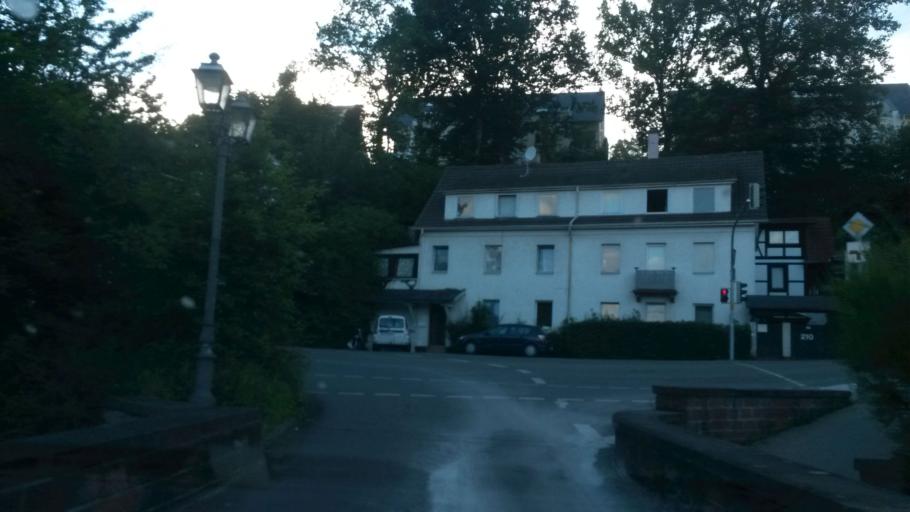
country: DE
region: Baden-Wuerttemberg
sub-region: Karlsruhe Region
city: Pforzheim
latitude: 48.8781
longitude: 8.6759
